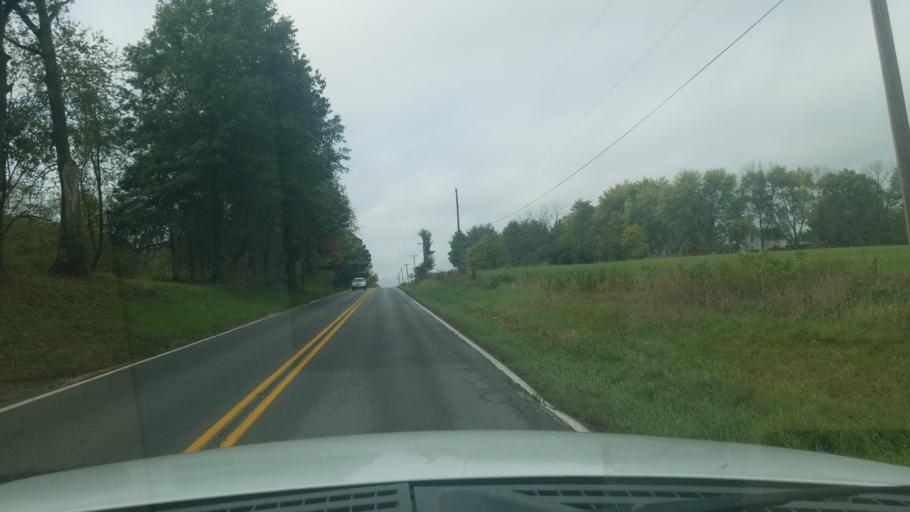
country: US
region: Illinois
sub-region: Saline County
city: Harrisburg
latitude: 37.8414
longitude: -88.6216
